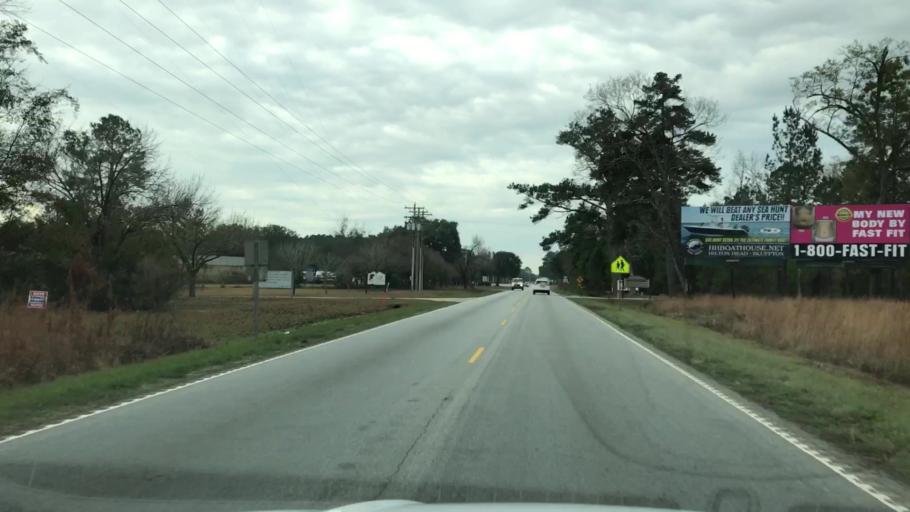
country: US
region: South Carolina
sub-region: Beaufort County
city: Bluffton
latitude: 32.3562
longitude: -80.9220
